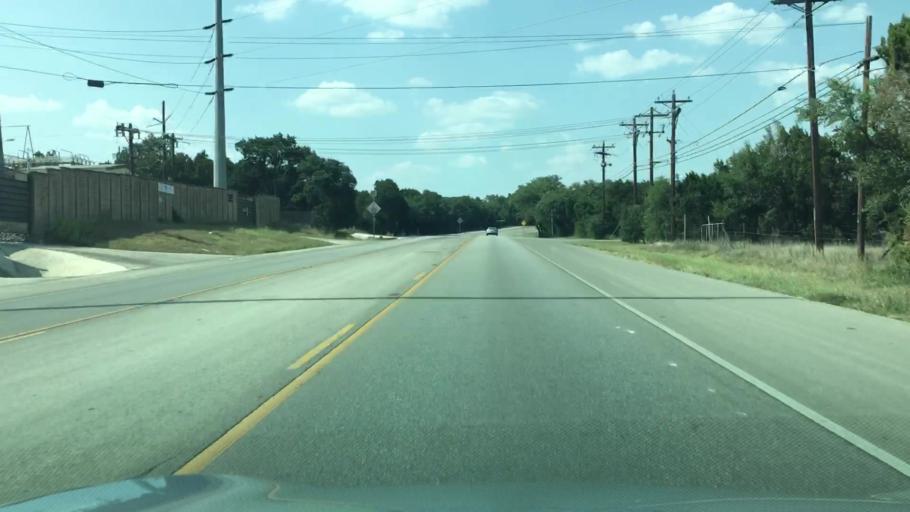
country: US
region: Texas
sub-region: Hays County
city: Wimberley
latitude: 29.9457
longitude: -98.0931
